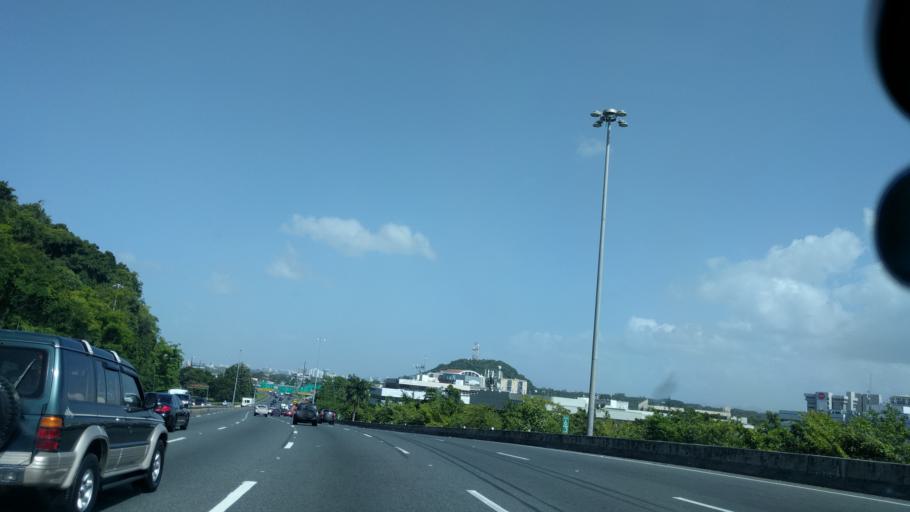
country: PR
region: Catano
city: Catano
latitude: 18.4176
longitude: -66.1068
